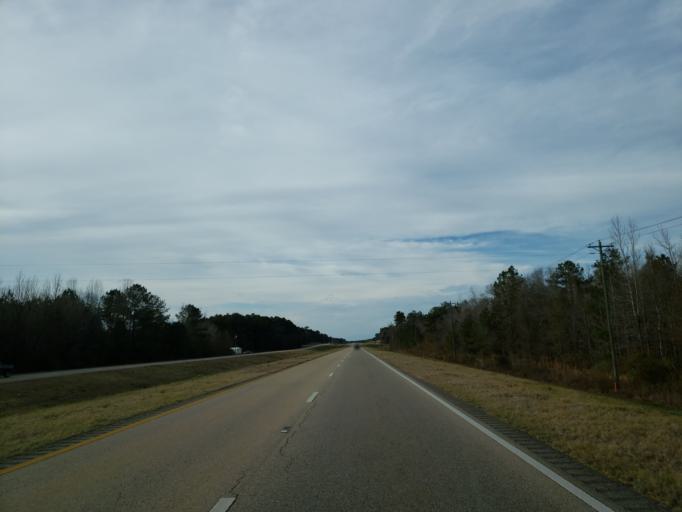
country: US
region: Mississippi
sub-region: Wayne County
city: Waynesboro
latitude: 31.6148
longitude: -88.5736
